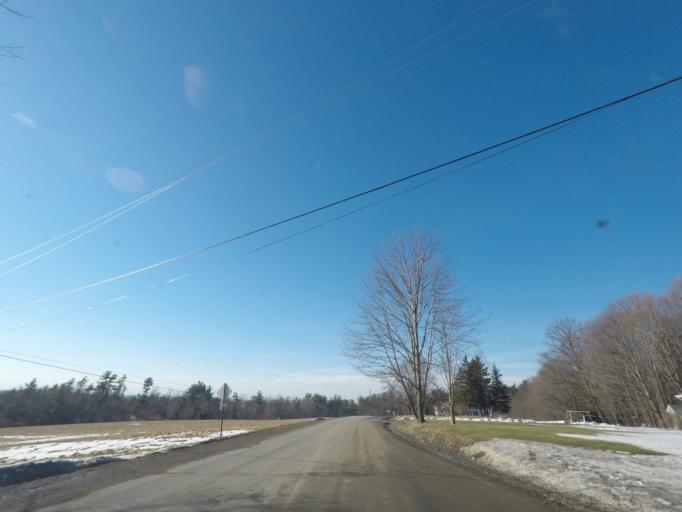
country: US
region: New York
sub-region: Rensselaer County
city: Averill Park
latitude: 42.6352
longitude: -73.5183
